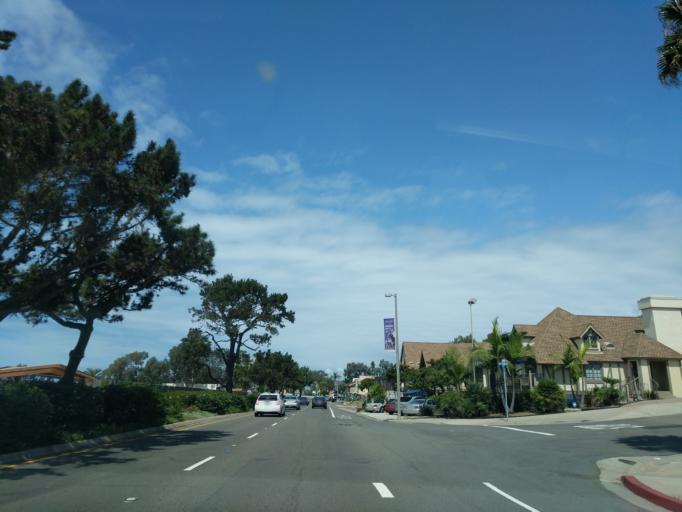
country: US
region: California
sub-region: San Diego County
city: Del Mar
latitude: 32.9542
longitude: -117.2632
